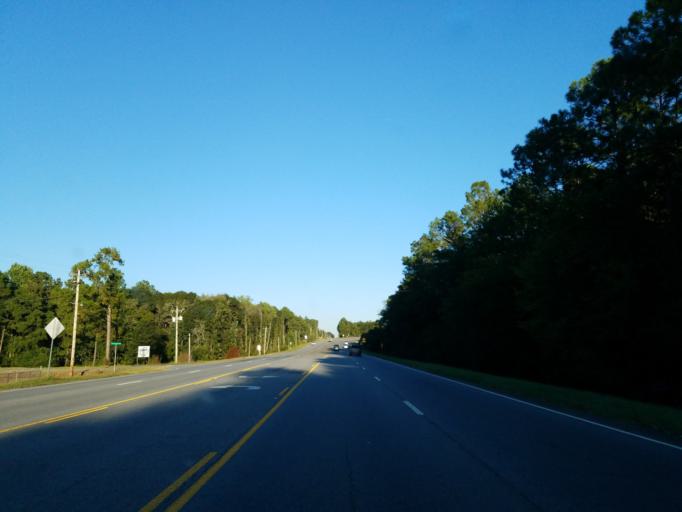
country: US
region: Georgia
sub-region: Worth County
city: Sylvester
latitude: 31.5274
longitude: -83.8026
